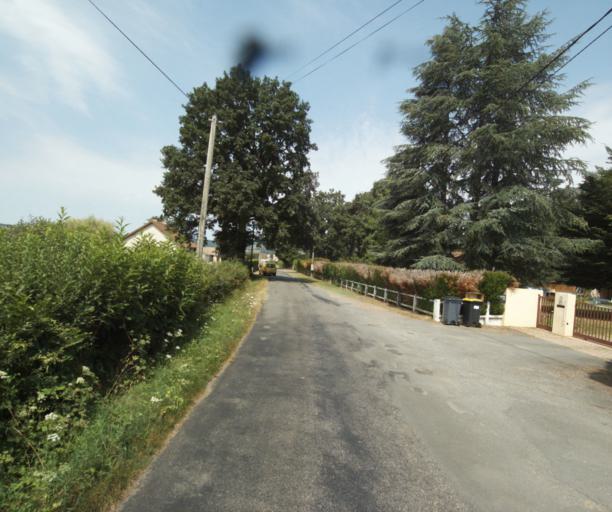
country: FR
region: Bourgogne
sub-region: Departement de Saone-et-Loire
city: Gueugnon
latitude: 46.5901
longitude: 4.0748
